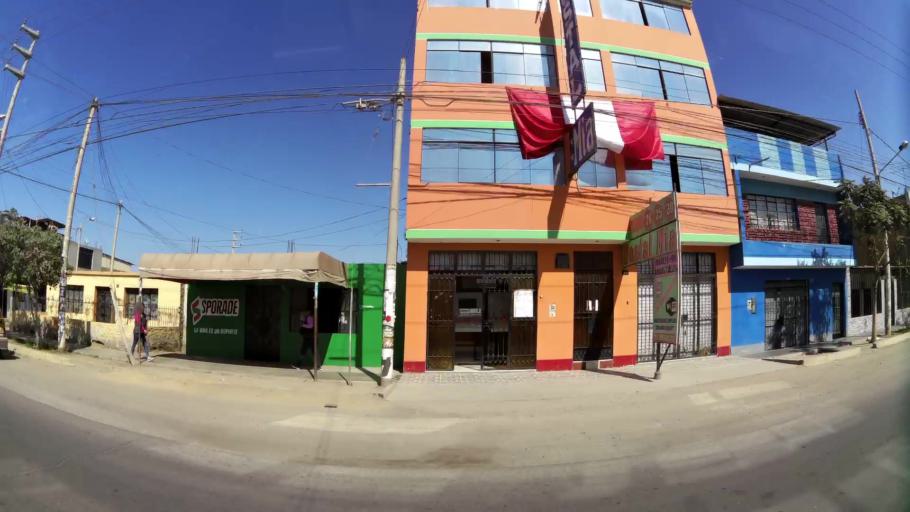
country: PE
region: Ica
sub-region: Provincia de Ica
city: La Tinguina
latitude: -14.0422
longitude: -75.7097
